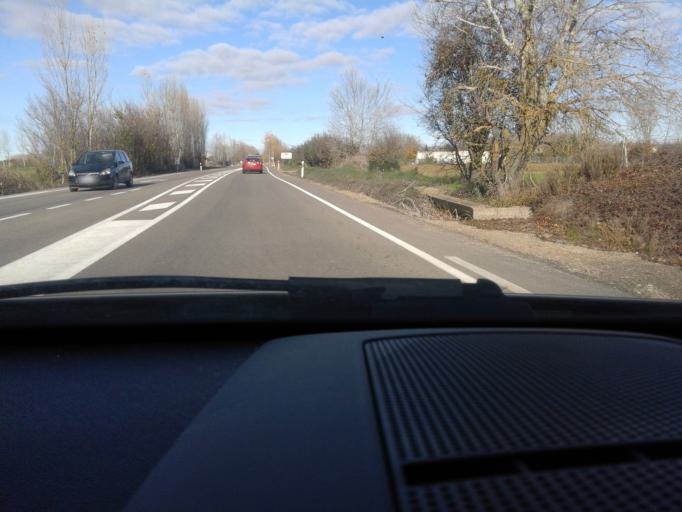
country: ES
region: Castille and Leon
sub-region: Provincia de Palencia
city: Carrion de los Condes
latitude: 42.3447
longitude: -4.6170
